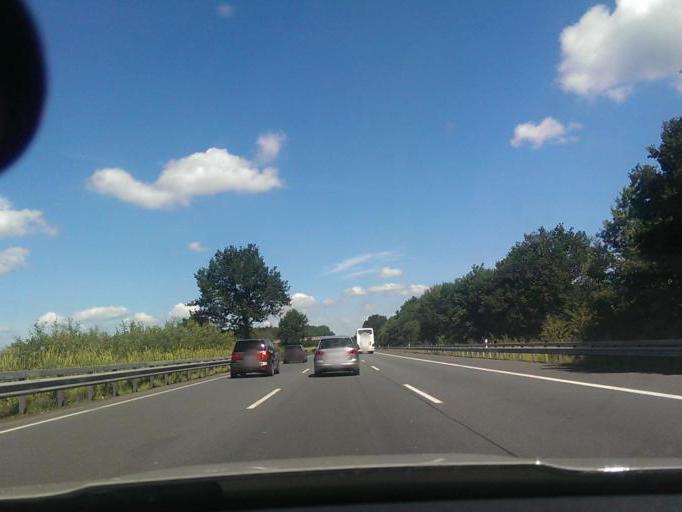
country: DE
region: Lower Saxony
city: Hademstorf
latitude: 52.7389
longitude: 9.6717
